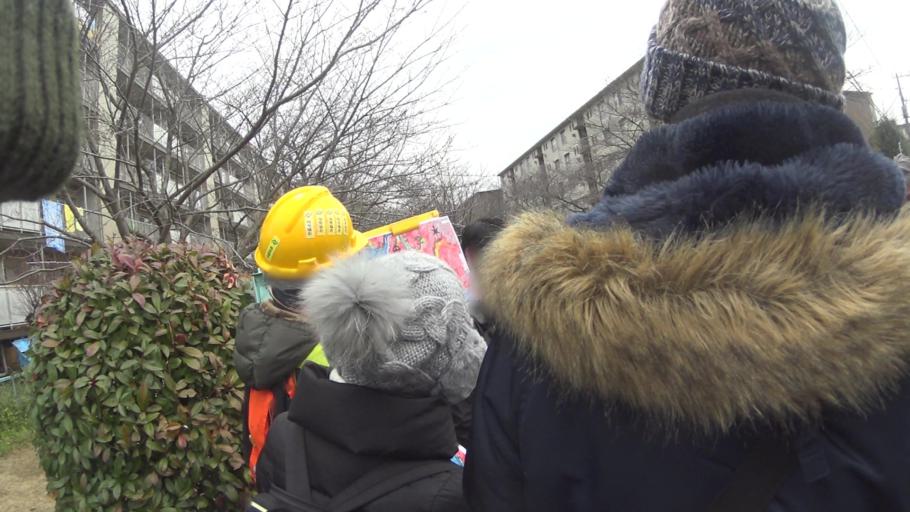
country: JP
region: Chiba
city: Funabashi
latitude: 35.7532
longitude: 139.9832
